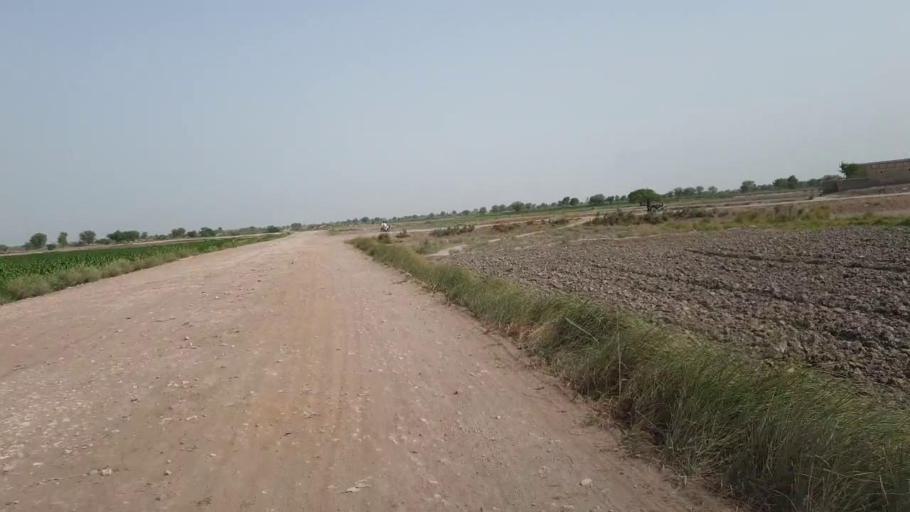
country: PK
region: Sindh
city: Daulatpur
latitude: 26.5524
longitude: 67.9914
